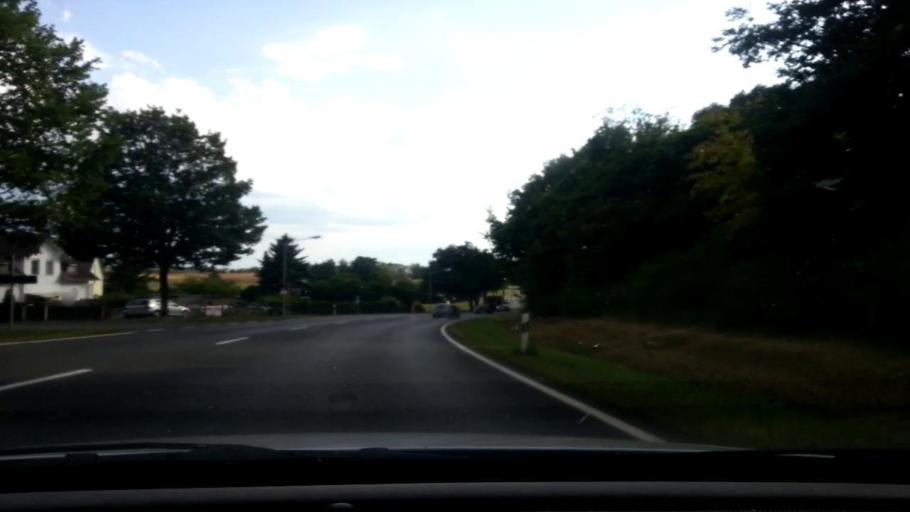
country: DE
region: Bavaria
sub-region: Upper Palatinate
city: Waldsassen
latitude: 49.9960
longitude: 12.2942
